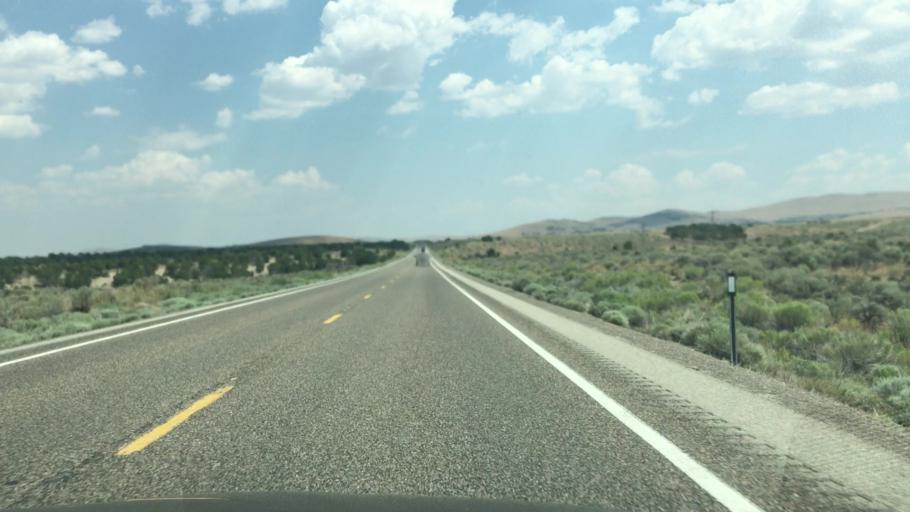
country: US
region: Nevada
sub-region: Elko County
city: Wells
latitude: 41.1966
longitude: -114.8622
